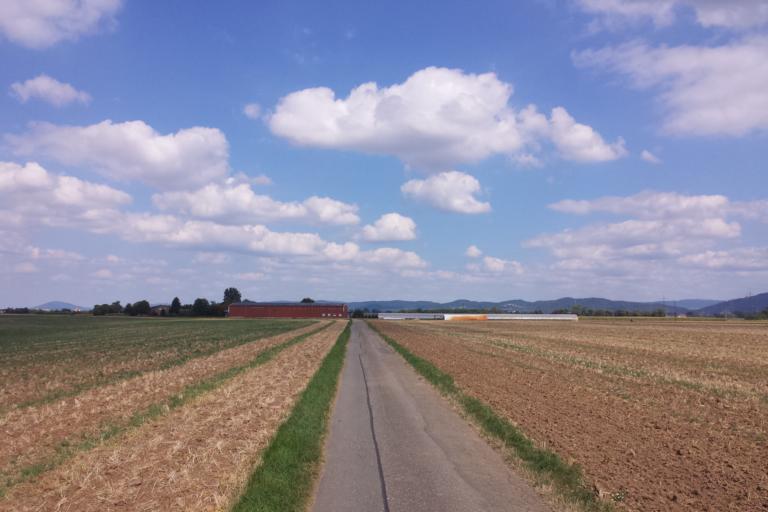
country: DE
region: Baden-Wuerttemberg
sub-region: Karlsruhe Region
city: Heddesheim
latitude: 49.5119
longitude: 8.5808
